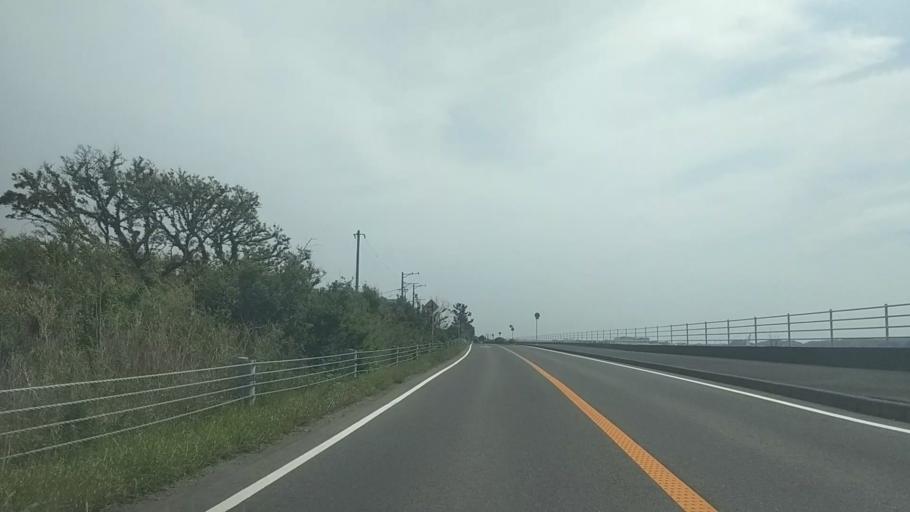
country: JP
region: Shizuoka
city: Kosai-shi
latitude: 34.7210
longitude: 137.5866
